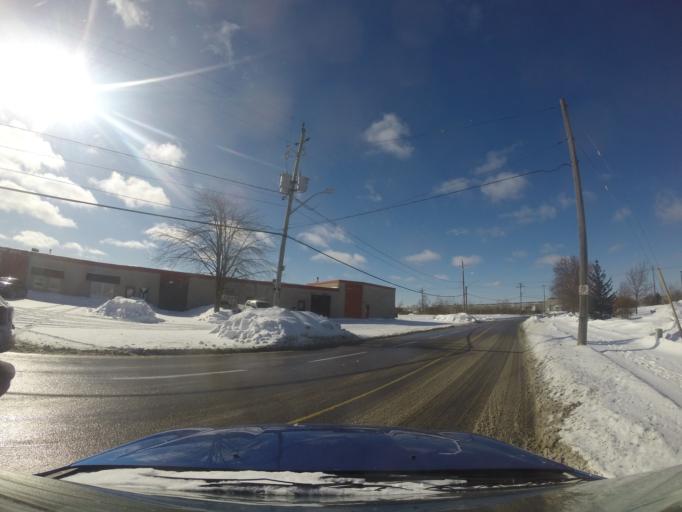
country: CA
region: Ontario
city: Cambridge
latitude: 43.4013
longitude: -80.3276
